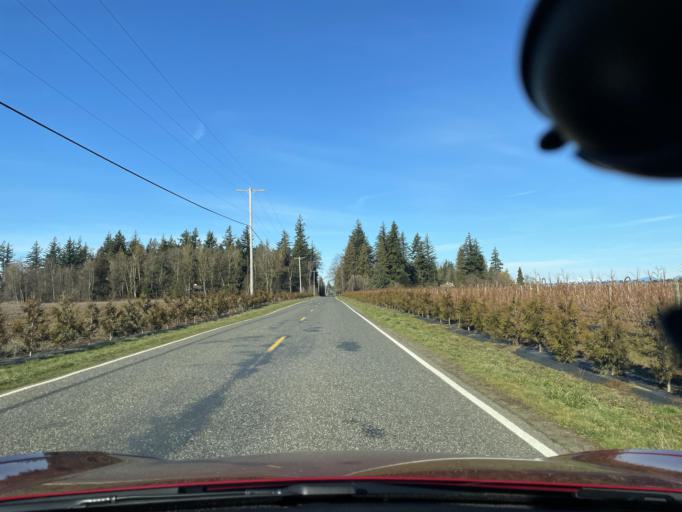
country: US
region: Washington
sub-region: Whatcom County
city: Lynden
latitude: 48.9541
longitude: -122.5303
